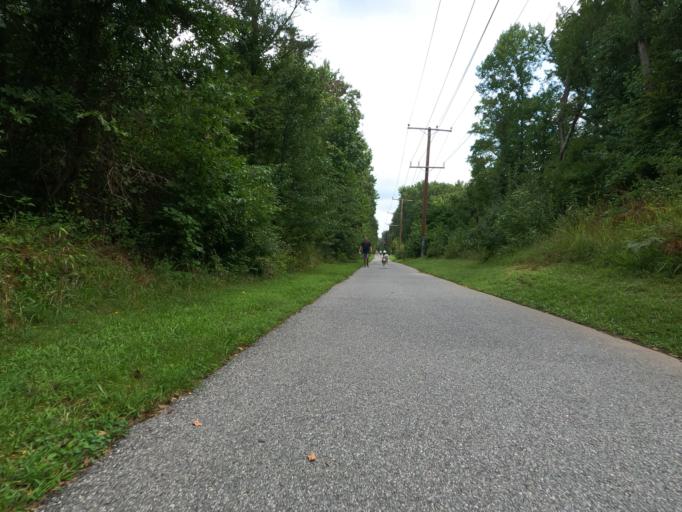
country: US
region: Maryland
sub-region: Anne Arundel County
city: Odenton
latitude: 39.0436
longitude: -76.7186
